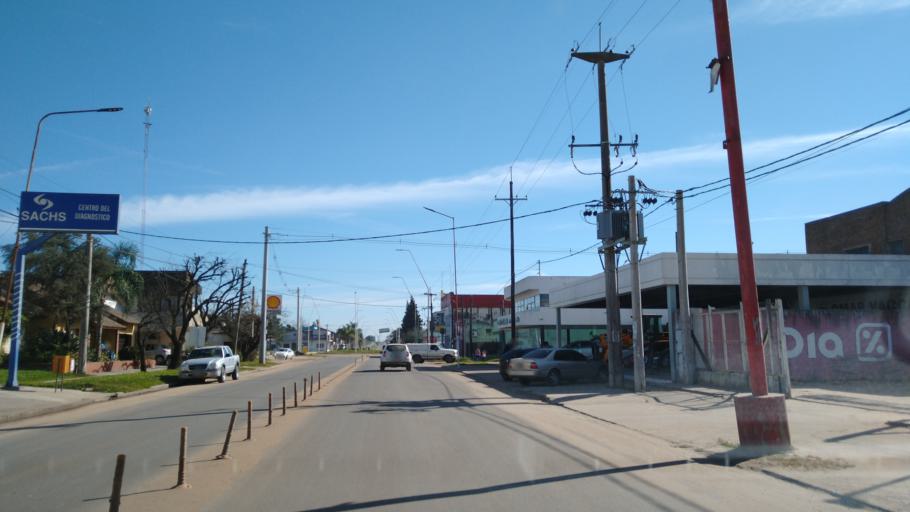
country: AR
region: Entre Rios
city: Chajari
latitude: -30.7613
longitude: -57.9965
